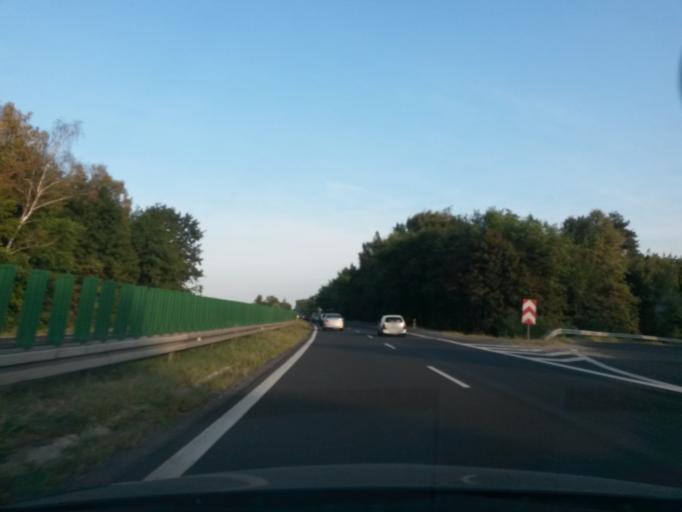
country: PL
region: Masovian Voivodeship
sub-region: Powiat nowodworski
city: Zakroczym
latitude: 52.4541
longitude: 20.5824
